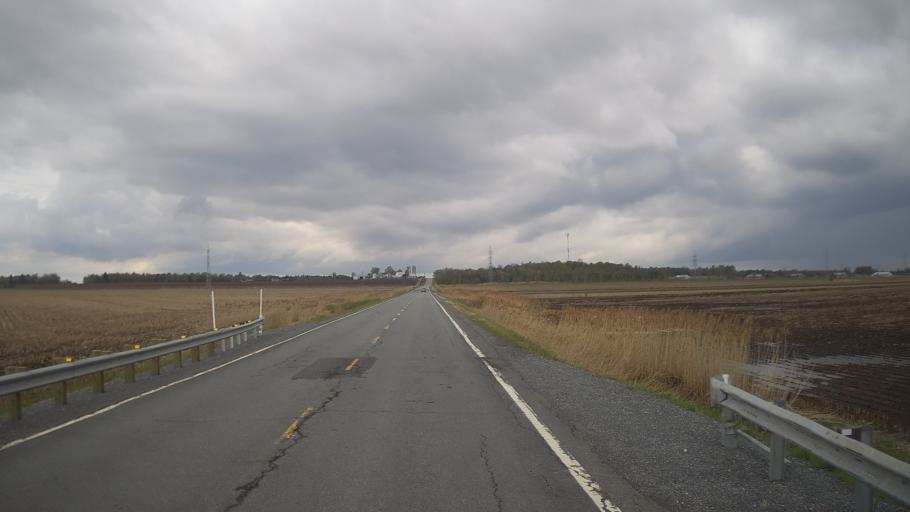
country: CA
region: Quebec
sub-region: Monteregie
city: Farnham
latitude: 45.2608
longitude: -72.9261
